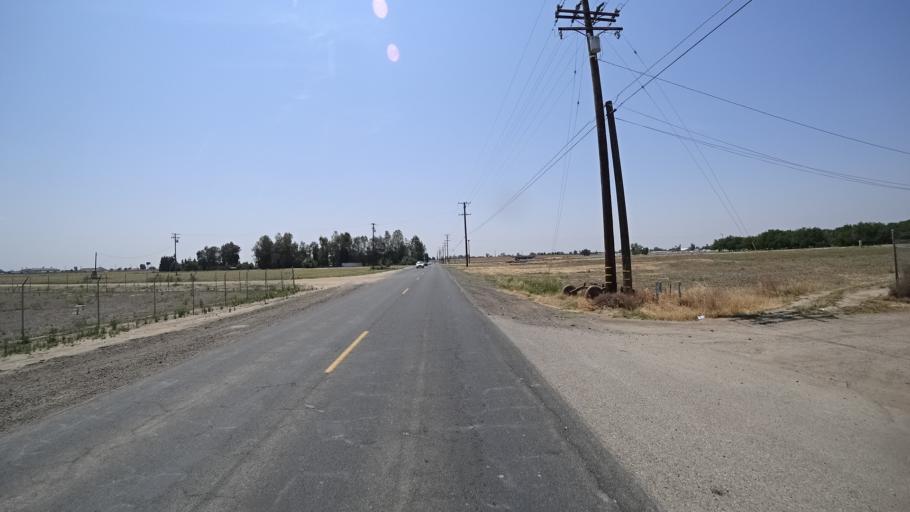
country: US
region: California
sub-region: Kings County
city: Armona
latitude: 36.3202
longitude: -119.6911
